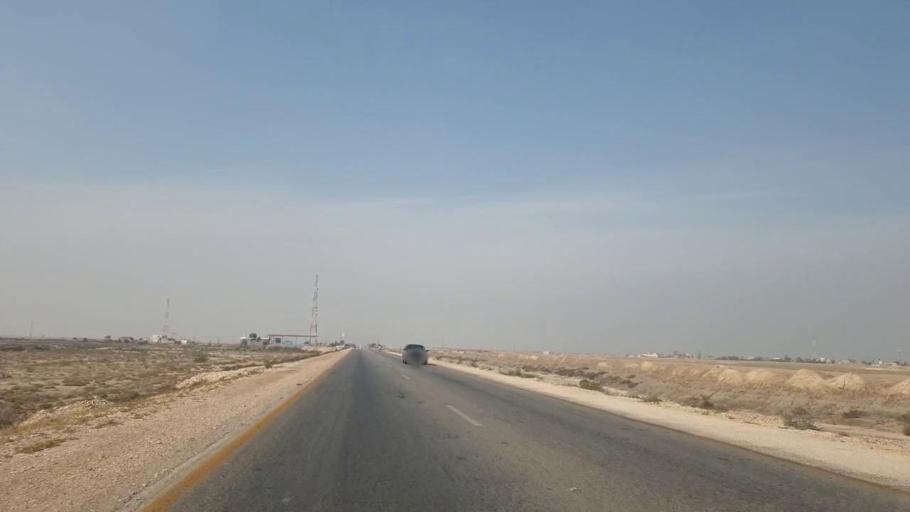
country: PK
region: Sindh
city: Sann
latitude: 25.8972
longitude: 68.2353
